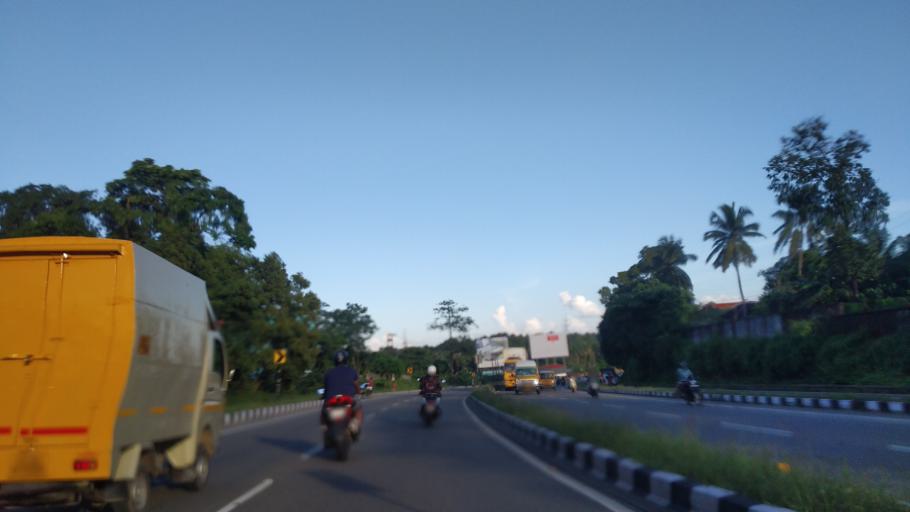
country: IN
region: Kerala
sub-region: Ernakulam
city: Elur
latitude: 10.0705
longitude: 76.3181
